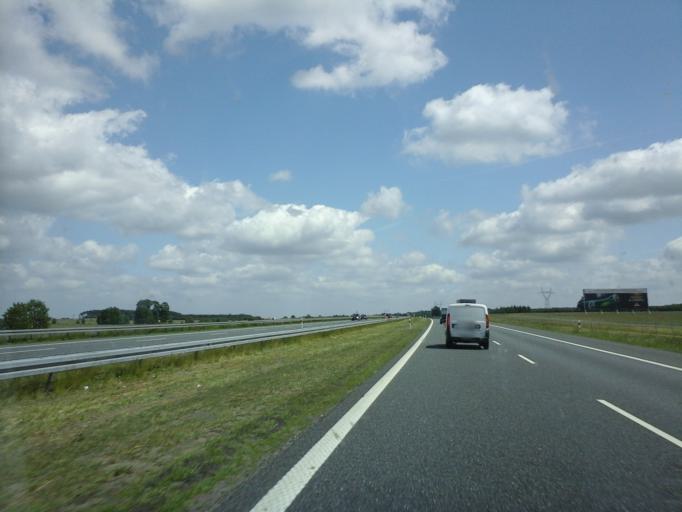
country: PL
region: Lodz Voivodeship
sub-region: Powiat zgierski
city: Ozorkow
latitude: 51.9308
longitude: 19.2866
